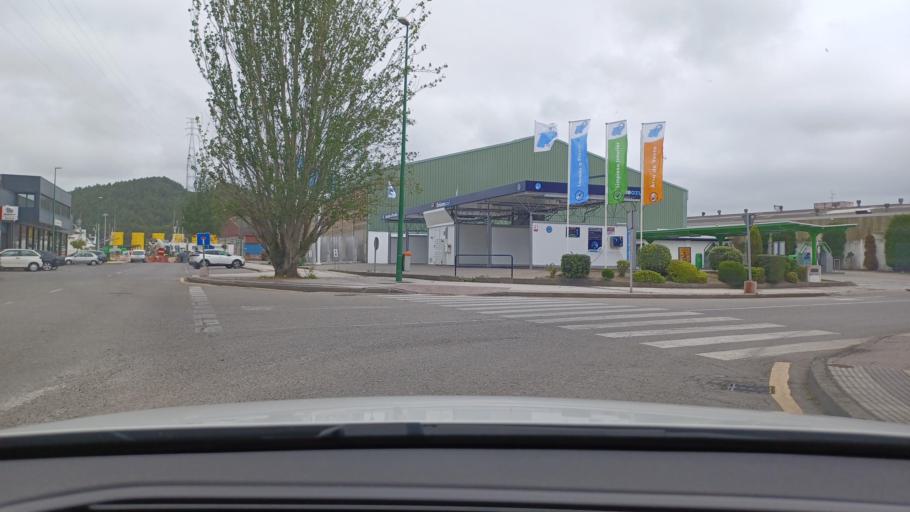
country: ES
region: Asturias
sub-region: Province of Asturias
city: Aviles
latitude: 43.5731
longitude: -5.9249
